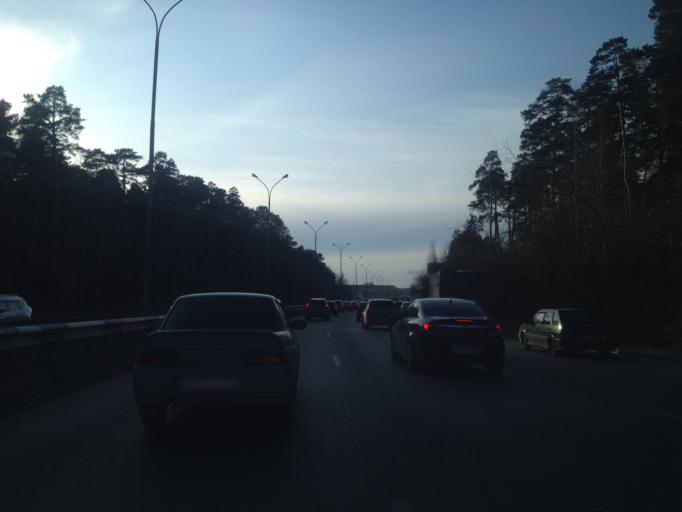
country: RU
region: Sverdlovsk
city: Sovkhoznyy
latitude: 56.7891
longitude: 60.5802
